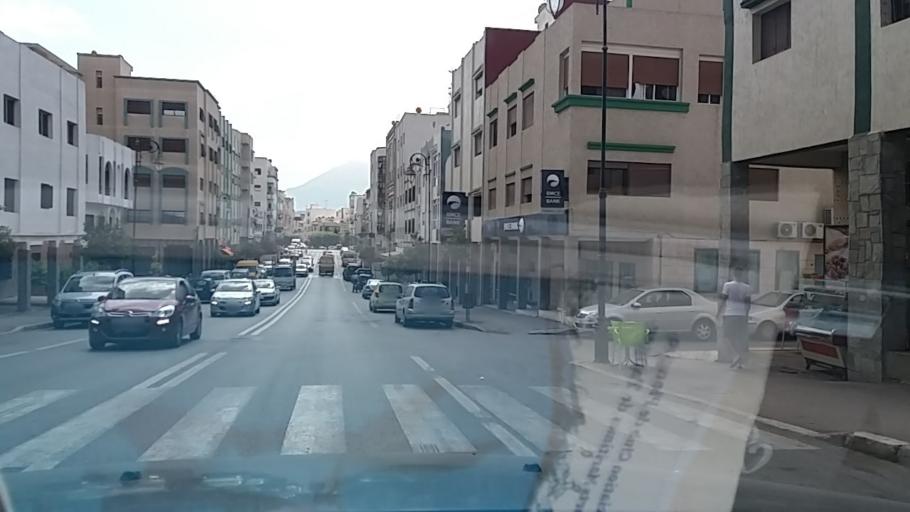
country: MA
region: Tanger-Tetouan
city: Tetouan
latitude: 35.5794
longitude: -5.3446
